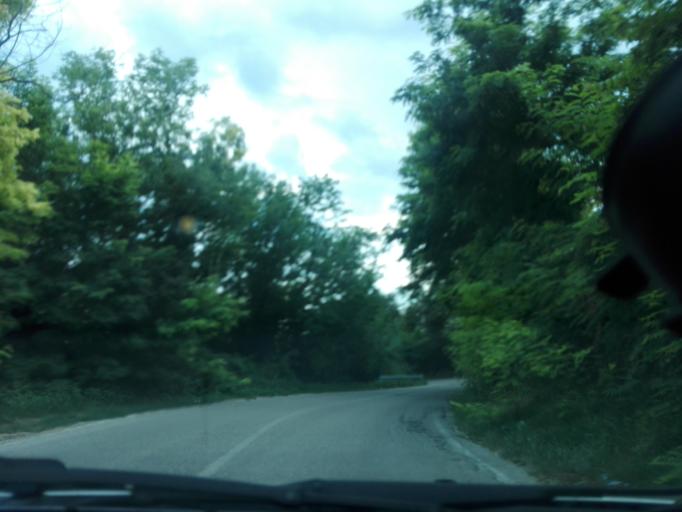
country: IT
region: Abruzzo
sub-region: Provincia di Pescara
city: Spoltore
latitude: 42.4756
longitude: 14.1367
